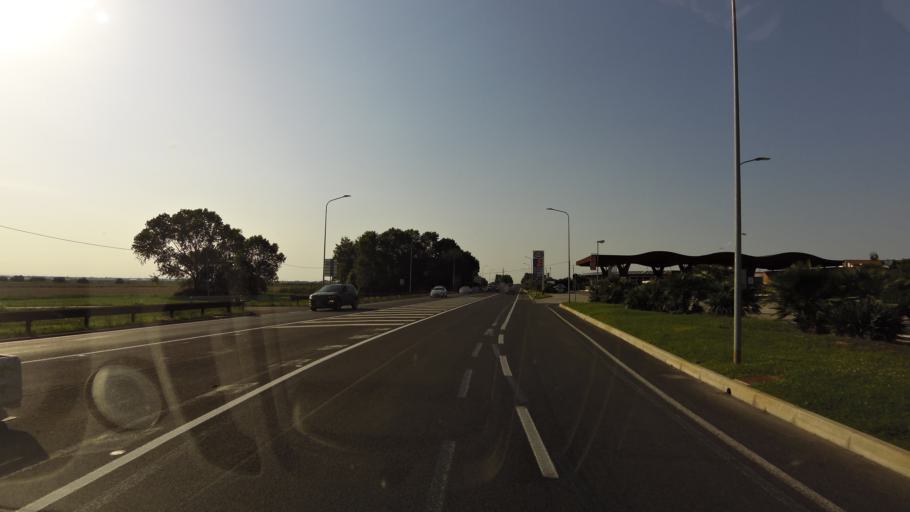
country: IT
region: Emilia-Romagna
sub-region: Provincia di Ravenna
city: Cervia
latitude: 44.2343
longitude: 12.3602
